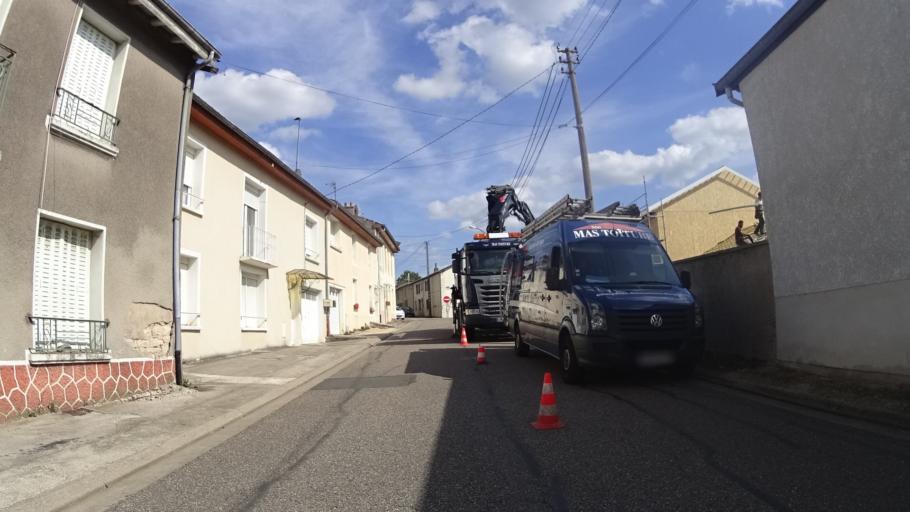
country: FR
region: Lorraine
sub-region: Departement de Meurthe-et-Moselle
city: Dommartin-les-Toul
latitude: 48.6539
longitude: 5.9044
